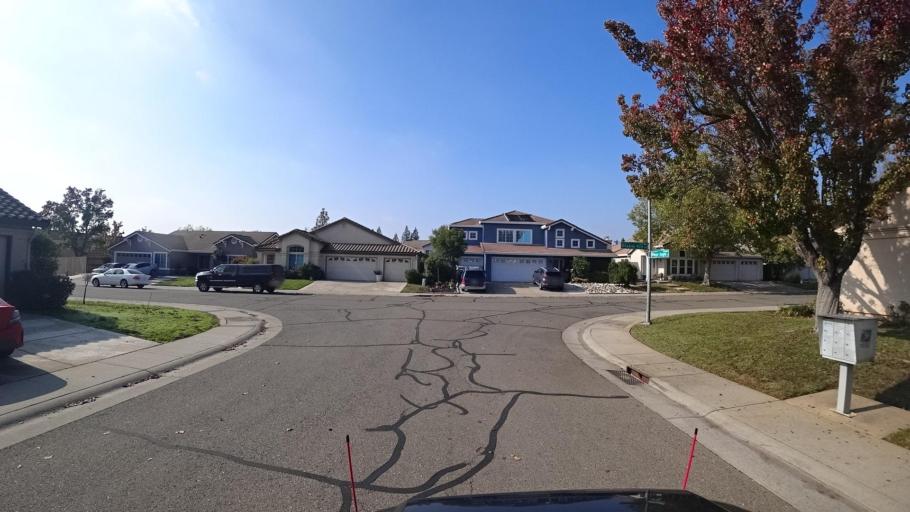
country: US
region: California
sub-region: Sacramento County
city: Vineyard
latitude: 38.4494
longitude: -121.3586
